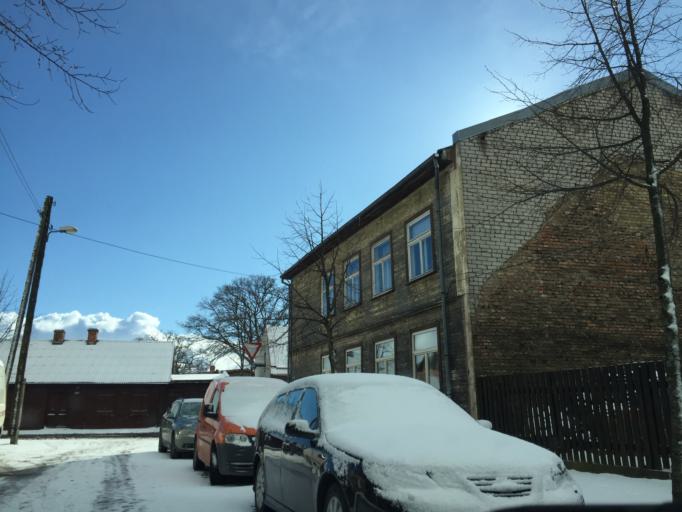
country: LV
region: Ventspils
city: Ventspils
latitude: 57.3922
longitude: 21.5588
